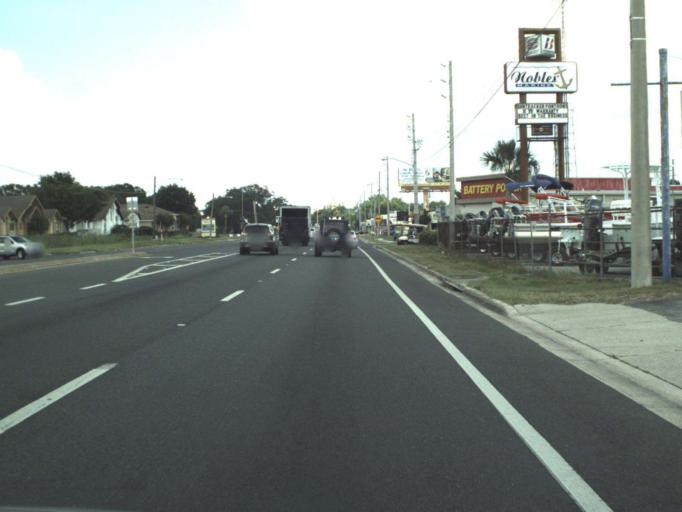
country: US
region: Florida
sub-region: Lake County
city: Leesburg
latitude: 28.8165
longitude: -81.8759
